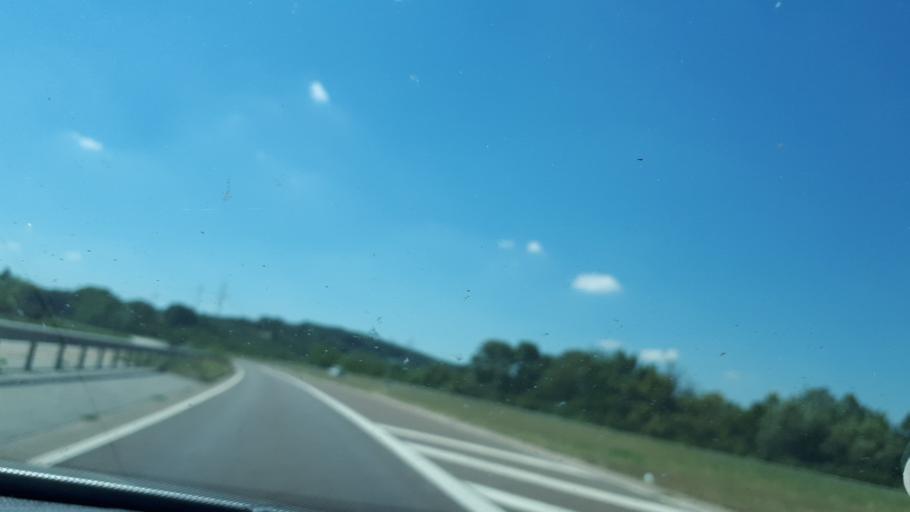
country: DE
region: Rheinland-Pfalz
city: Kaltenengers
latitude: 50.3918
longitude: 7.5426
